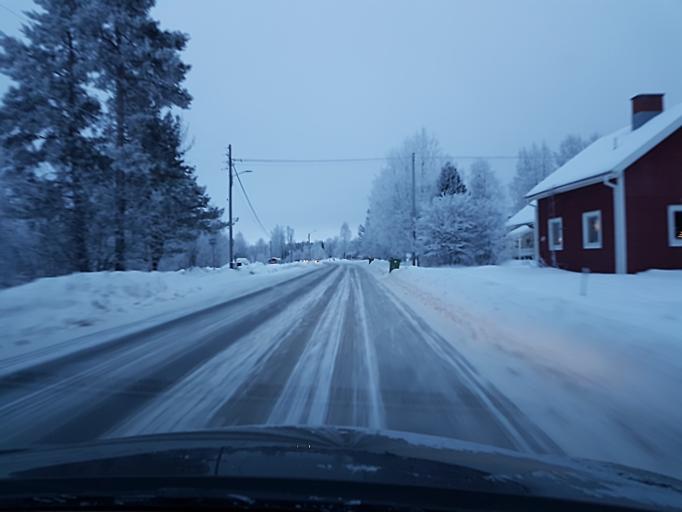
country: SE
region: Norrbotten
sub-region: Pitea Kommun
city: Roknas
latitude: 65.3452
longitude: 21.1256
